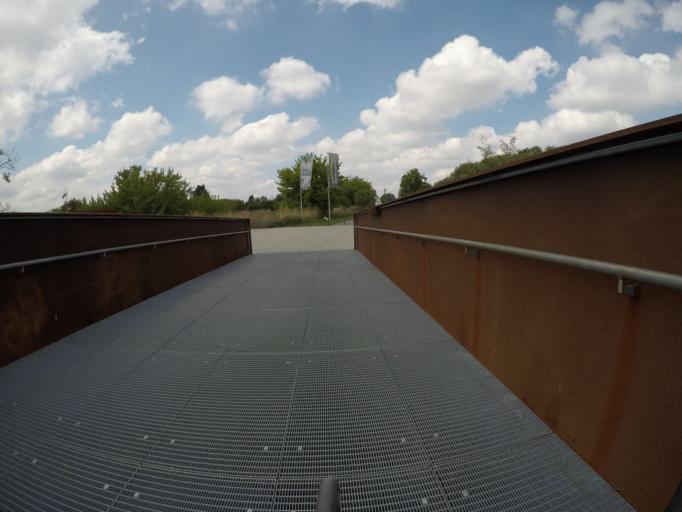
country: DE
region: Berlin
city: Kaulsdorf
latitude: 52.5307
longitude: 13.5829
